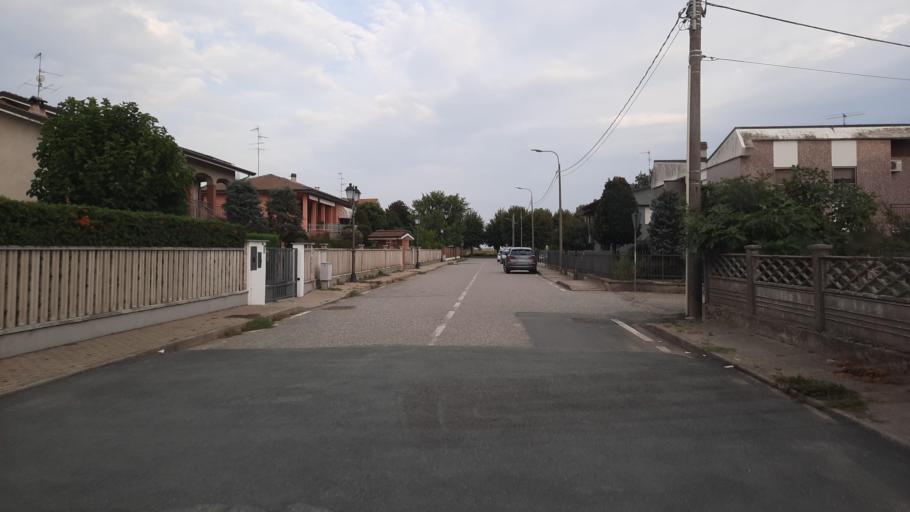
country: IT
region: Piedmont
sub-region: Provincia di Vercelli
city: Lignana
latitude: 45.2880
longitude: 8.3455
